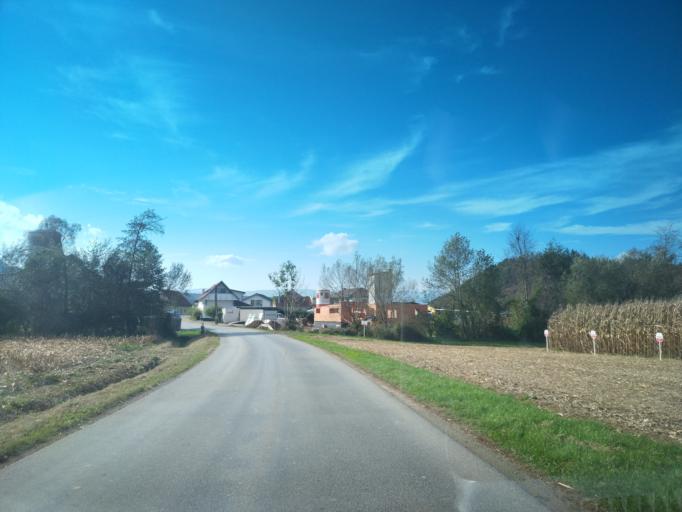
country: AT
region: Styria
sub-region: Politischer Bezirk Leibnitz
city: Oberhaag
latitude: 46.6865
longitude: 15.3582
